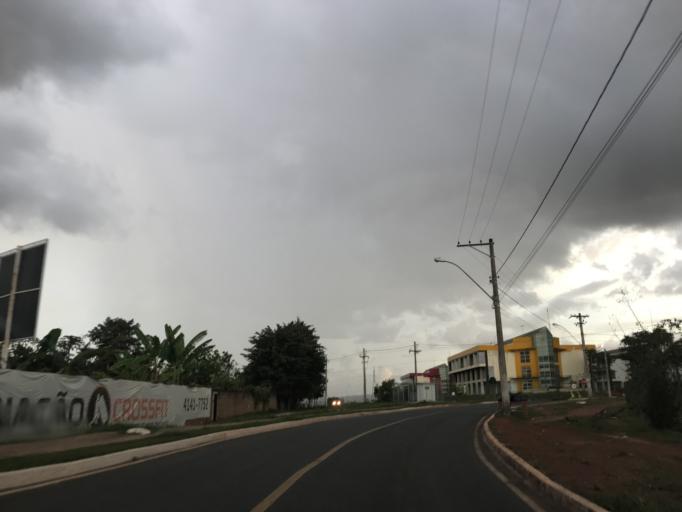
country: BR
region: Federal District
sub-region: Brasilia
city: Brasilia
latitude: -15.8336
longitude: -48.0086
